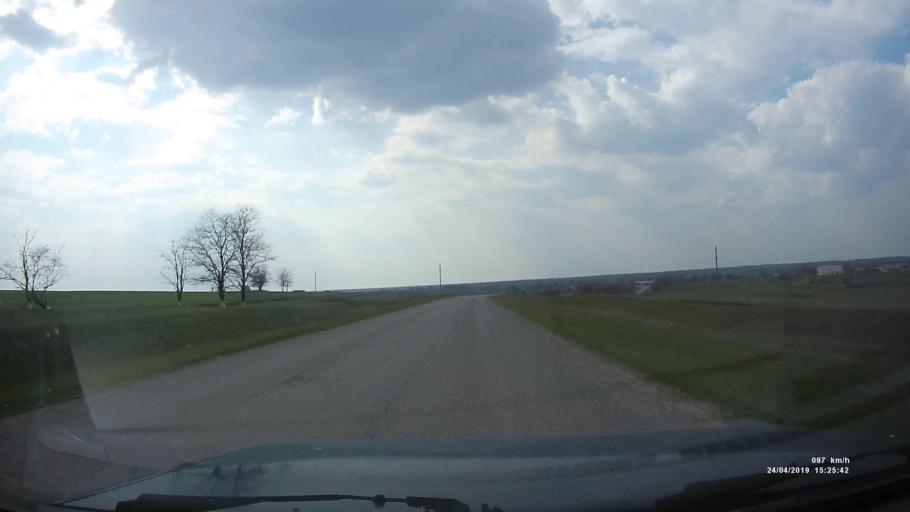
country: RU
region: Rostov
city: Remontnoye
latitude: 46.5535
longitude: 43.0425
